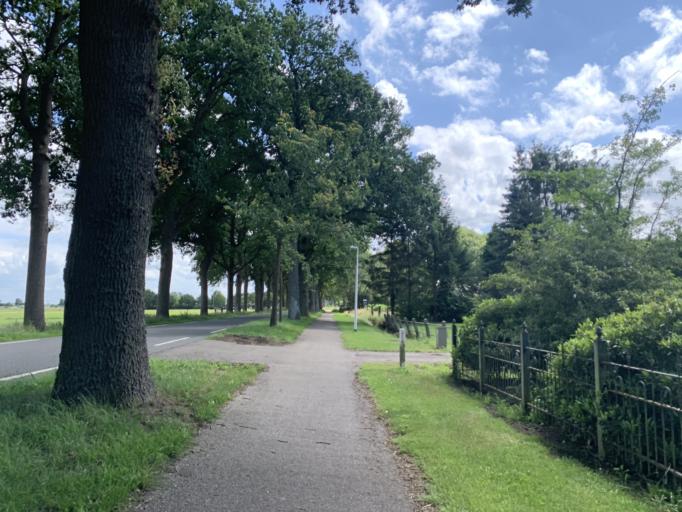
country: NL
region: Drenthe
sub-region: Gemeente Tynaarlo
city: Zuidlaren
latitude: 53.1391
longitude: 6.6526
